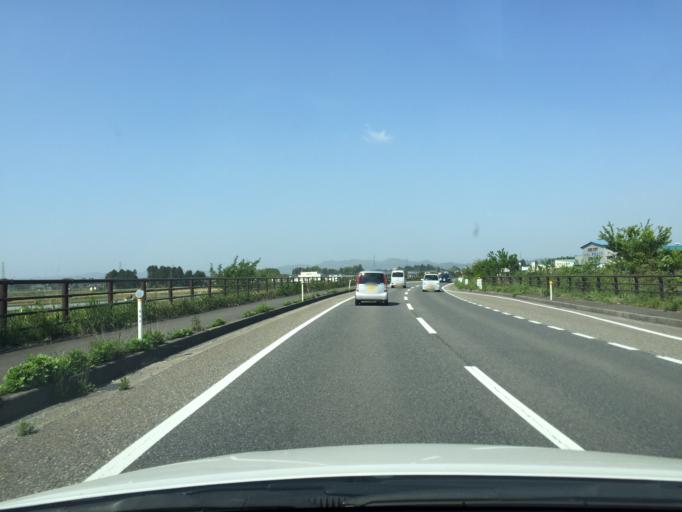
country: JP
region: Niigata
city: Gosen
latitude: 37.7484
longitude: 139.2154
